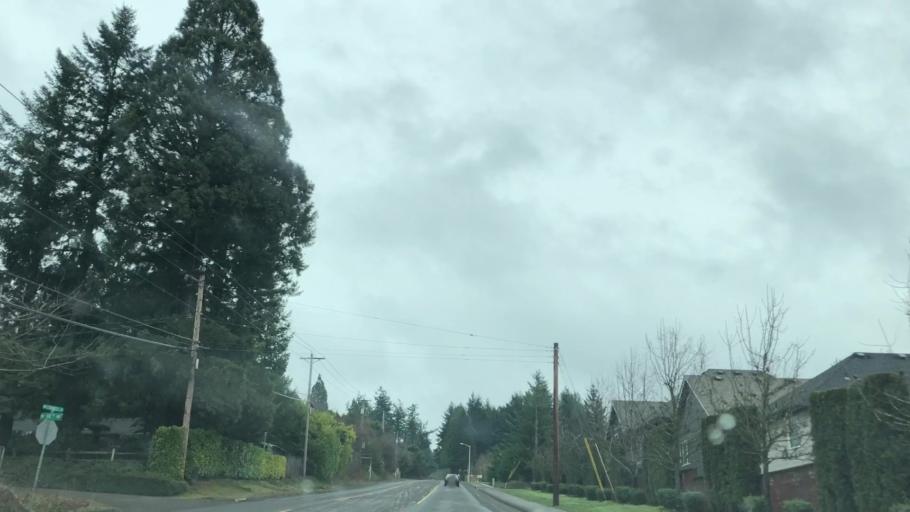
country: US
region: Oregon
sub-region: Washington County
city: West Haven
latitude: 45.5280
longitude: -122.7740
